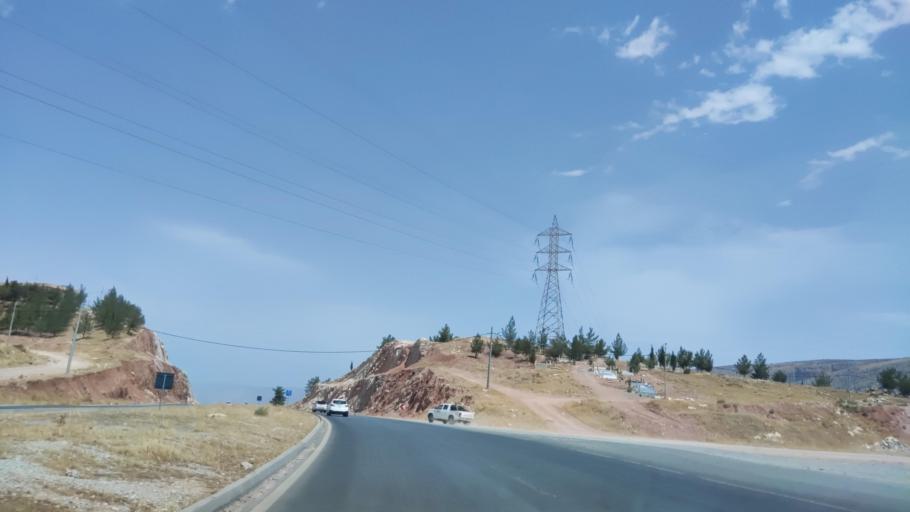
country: IQ
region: Arbil
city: Shaqlawah
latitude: 36.4868
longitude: 44.3811
